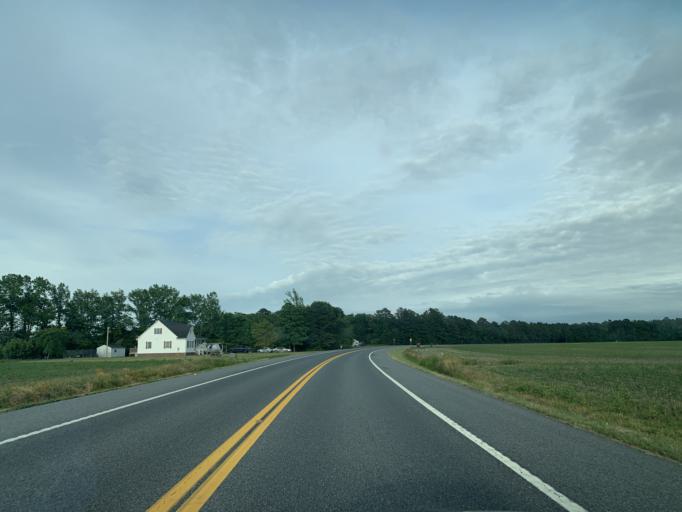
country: US
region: Virginia
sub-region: Accomack County
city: Captains Cove
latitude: 38.0676
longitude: -75.4341
